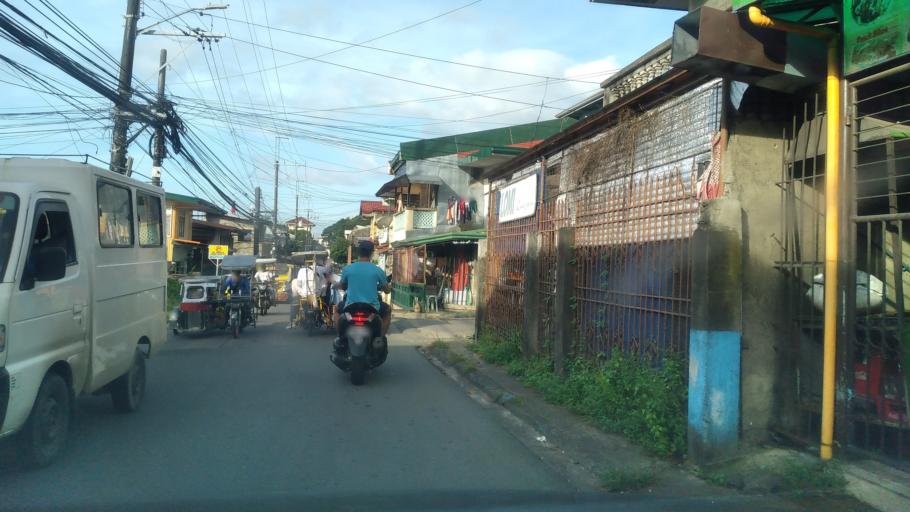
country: PH
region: Calabarzon
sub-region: Province of Quezon
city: Sariaya
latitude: 13.9634
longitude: 121.5268
